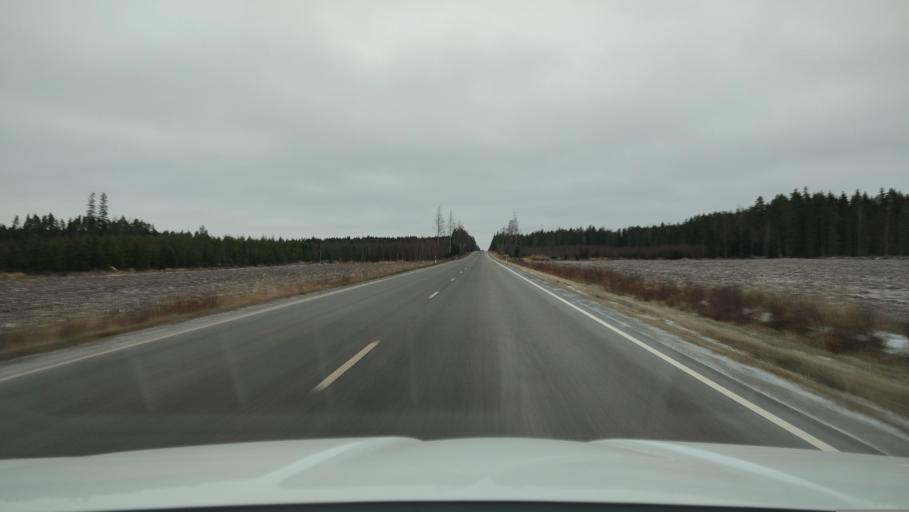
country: FI
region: Ostrobothnia
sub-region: Sydosterbotten
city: Naerpes
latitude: 62.4867
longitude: 21.4423
